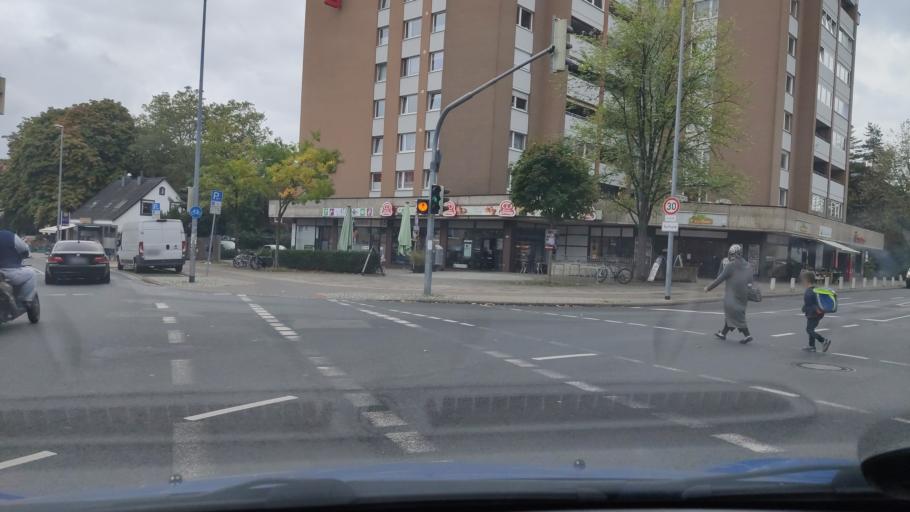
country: DE
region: Lower Saxony
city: Ronnenberg
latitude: 52.3844
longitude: 9.6637
